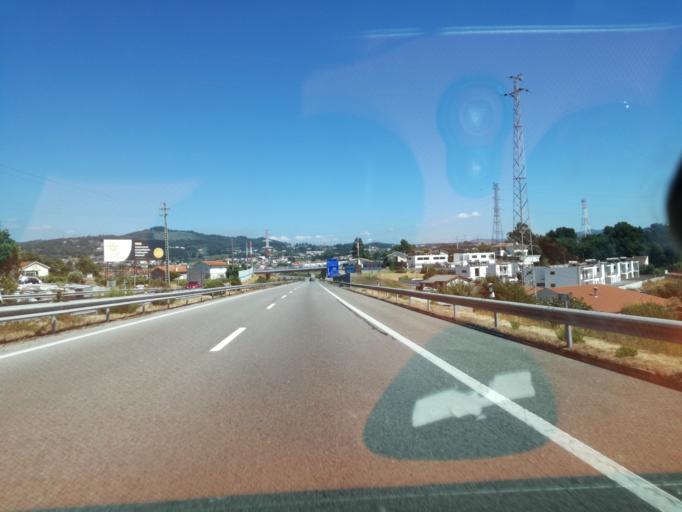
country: PT
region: Braga
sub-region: Guimaraes
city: Serzedelo
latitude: 41.4070
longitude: -8.3942
